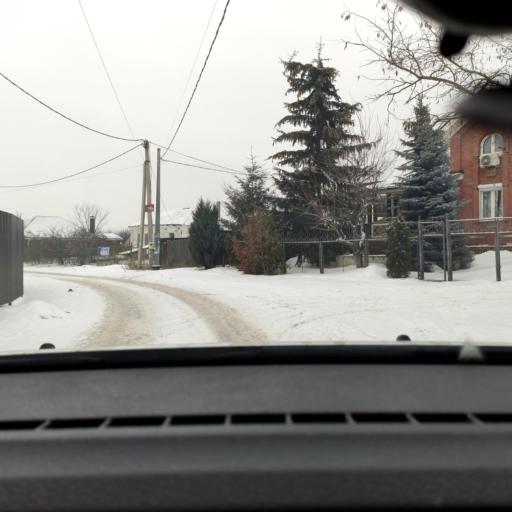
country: RU
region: Voronezj
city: Podgornoye
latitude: 51.7954
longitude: 39.1405
